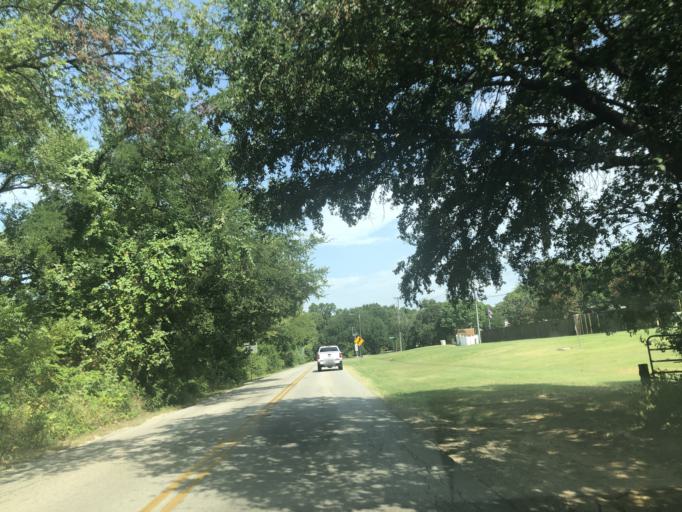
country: US
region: Texas
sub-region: Dallas County
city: Grand Prairie
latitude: 32.7679
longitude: -97.0400
